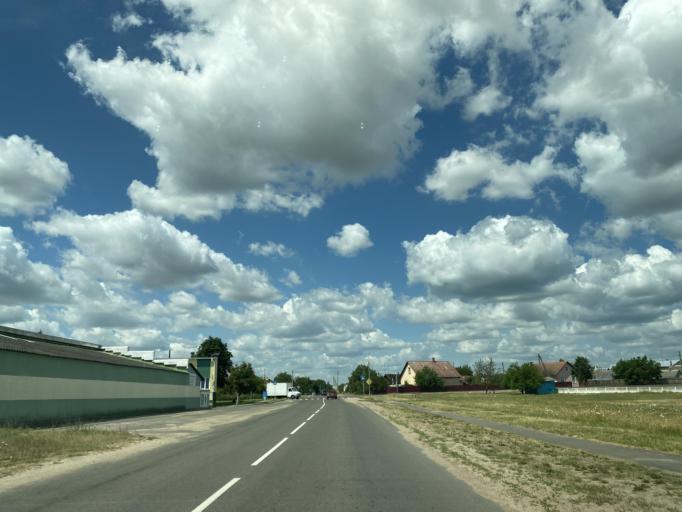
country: BY
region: Brest
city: Ivanava
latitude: 52.1409
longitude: 25.5496
